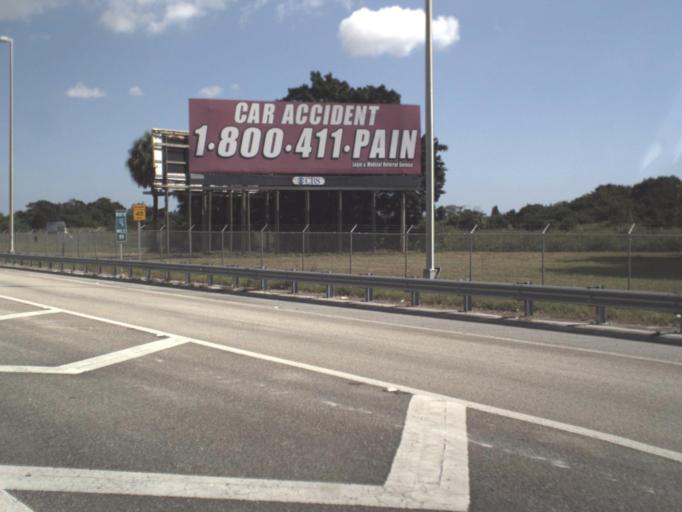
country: US
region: Florida
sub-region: Palm Beach County
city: Lake Belvedere Estates
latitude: 26.6963
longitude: -80.1520
